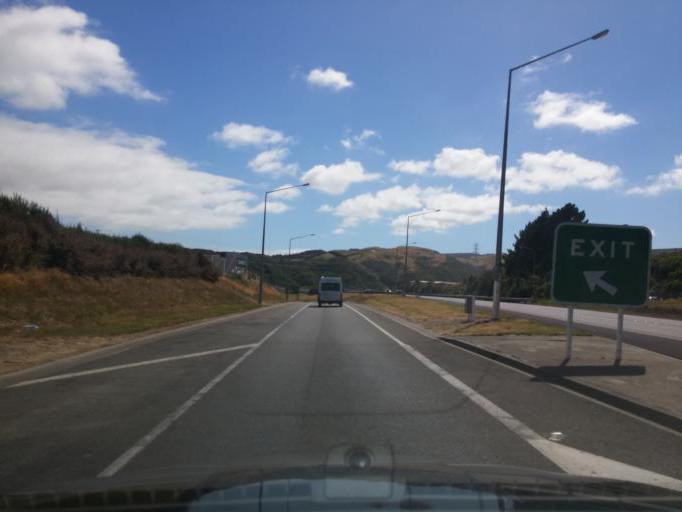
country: NZ
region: Wellington
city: Petone
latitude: -41.1880
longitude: 174.8315
